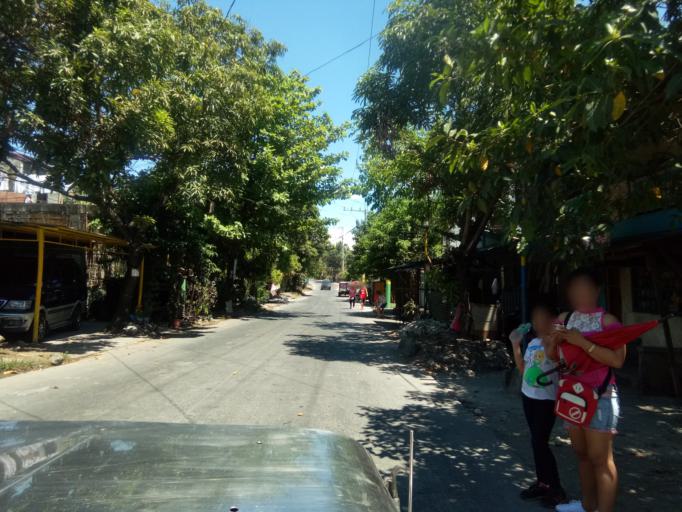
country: PH
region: Calabarzon
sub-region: Province of Cavite
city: Dasmarinas
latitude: 14.3209
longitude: 120.9682
